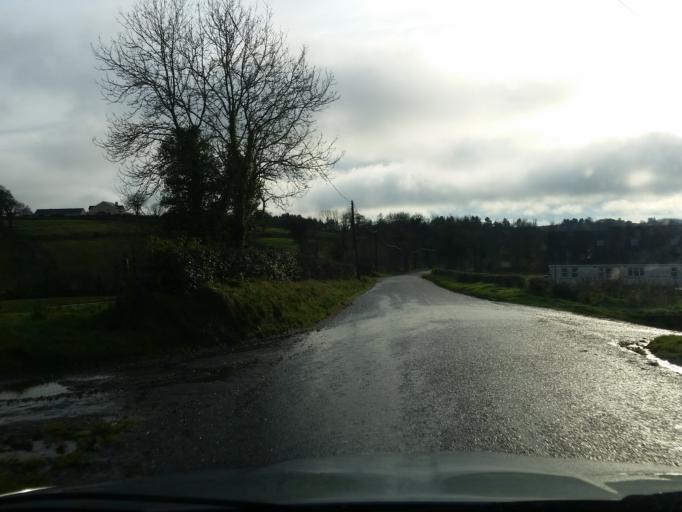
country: GB
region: Northern Ireland
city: Lisnaskea
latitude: 54.2593
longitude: -7.3810
